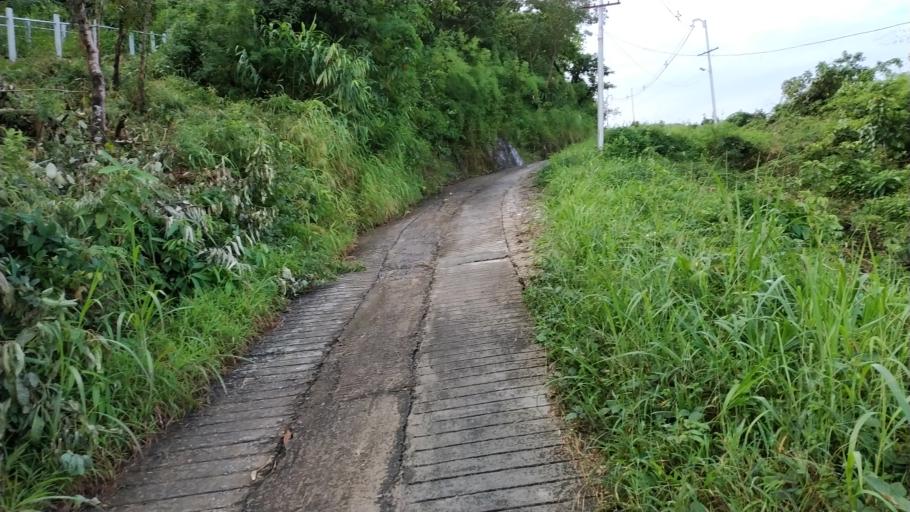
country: MM
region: Mon
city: Thaton
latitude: 16.9262
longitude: 97.3818
